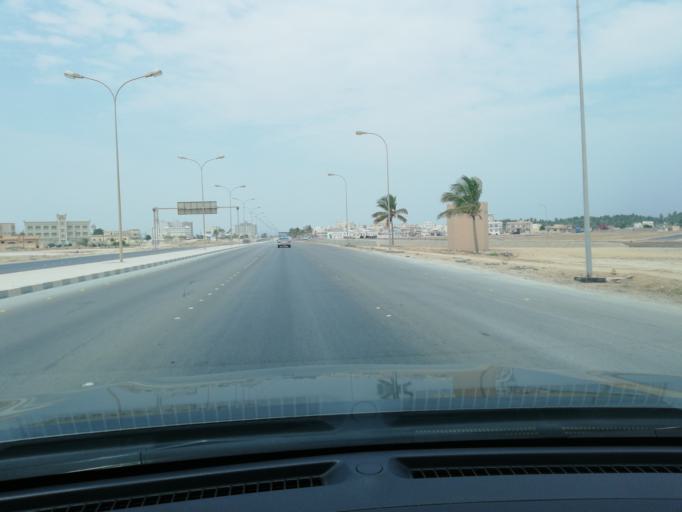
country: OM
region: Zufar
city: Salalah
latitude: 16.9969
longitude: 54.0326
